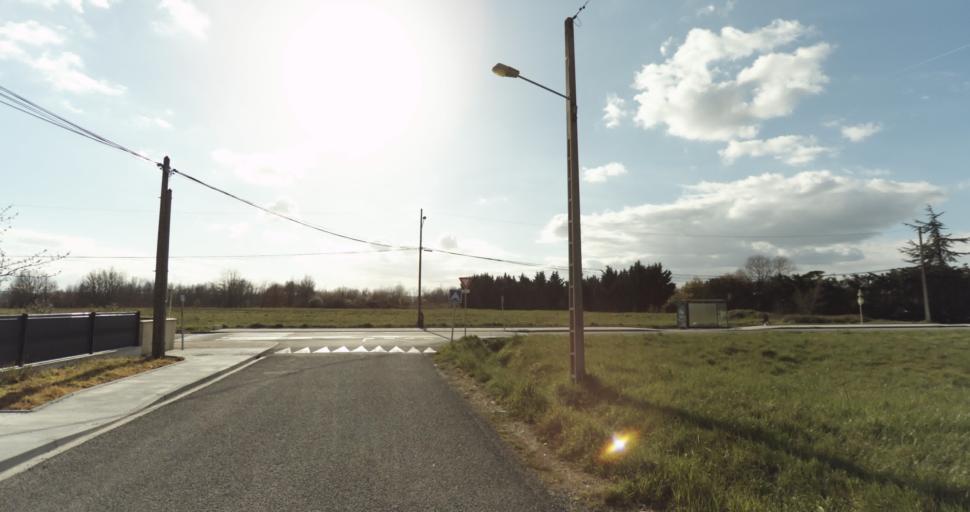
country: FR
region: Midi-Pyrenees
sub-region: Departement de la Haute-Garonne
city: Auterive
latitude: 43.3435
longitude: 1.4854
